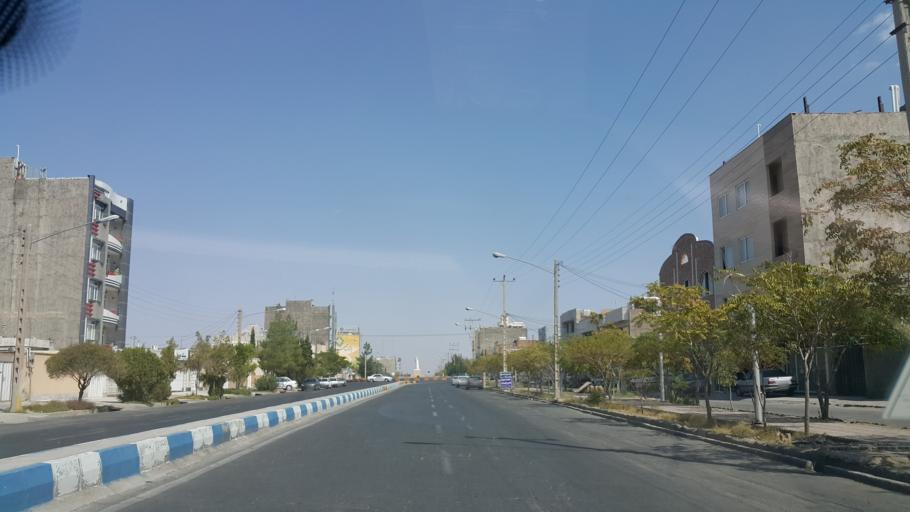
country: IR
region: Khorasan-e Jonubi
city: Birjand
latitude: 32.8462
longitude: 59.2161
